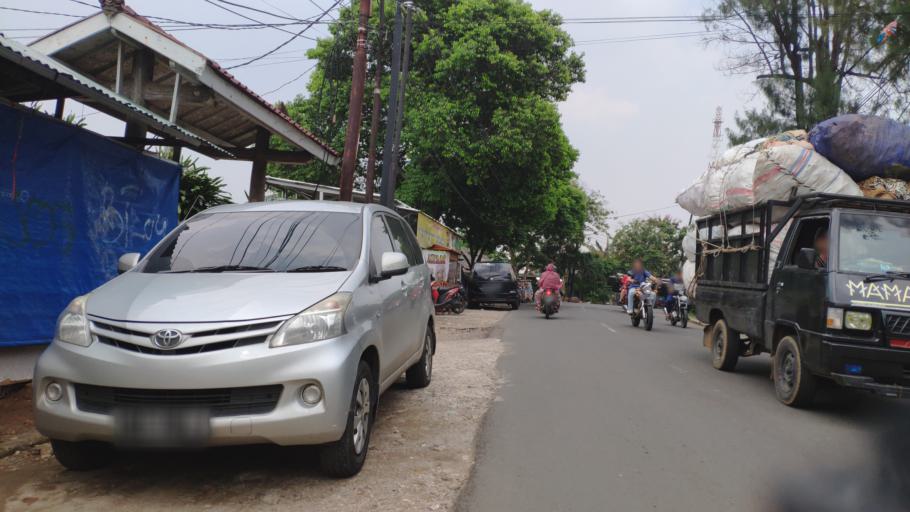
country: ID
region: West Java
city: Depok
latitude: -6.3449
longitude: 106.8278
